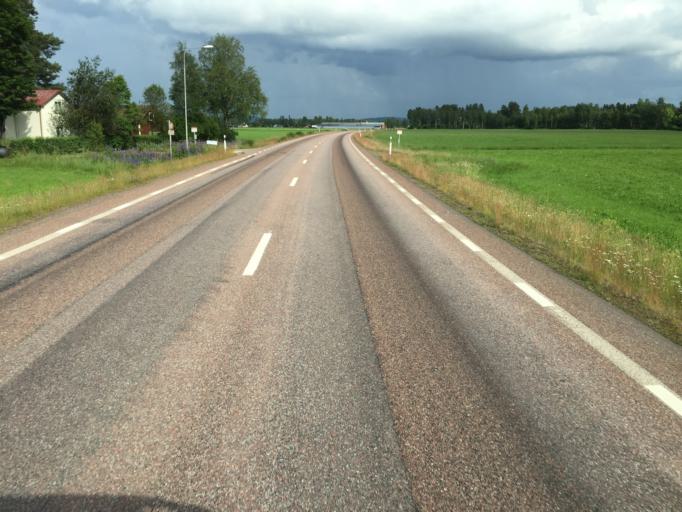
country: SE
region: Dalarna
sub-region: Vansbro Kommun
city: Jarna
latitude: 60.5544
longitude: 14.3394
